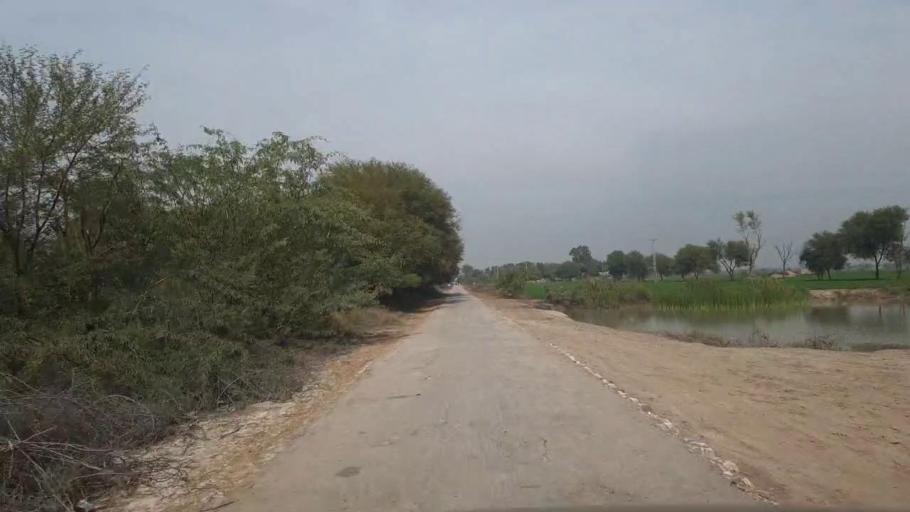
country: PK
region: Sindh
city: Nawabshah
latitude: 26.1195
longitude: 68.4800
